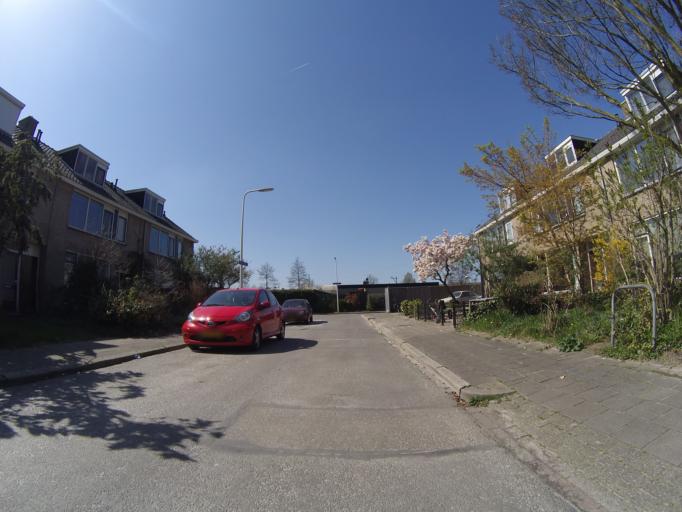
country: NL
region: Utrecht
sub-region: Gemeente Amersfoort
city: Amersfoort
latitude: 52.1695
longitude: 5.3991
